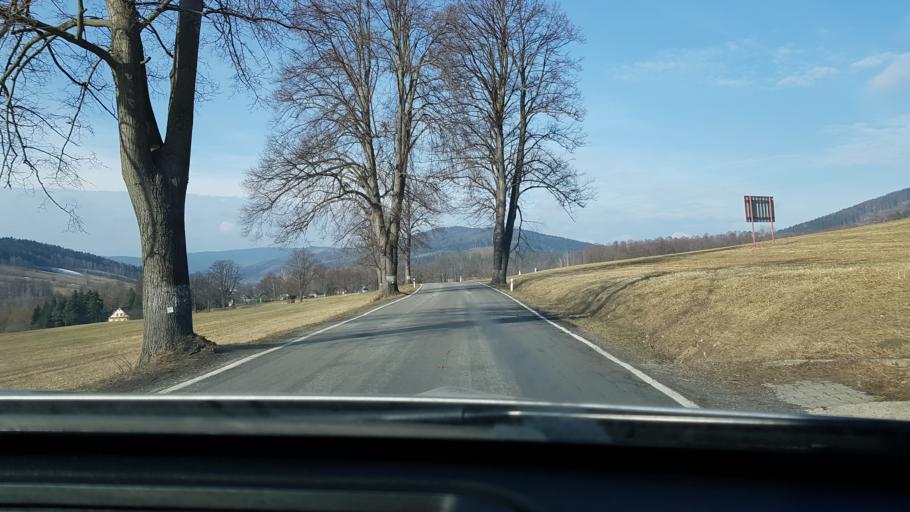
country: CZ
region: Olomoucky
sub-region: Okres Jesenik
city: Jesenik
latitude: 50.2284
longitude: 17.1761
